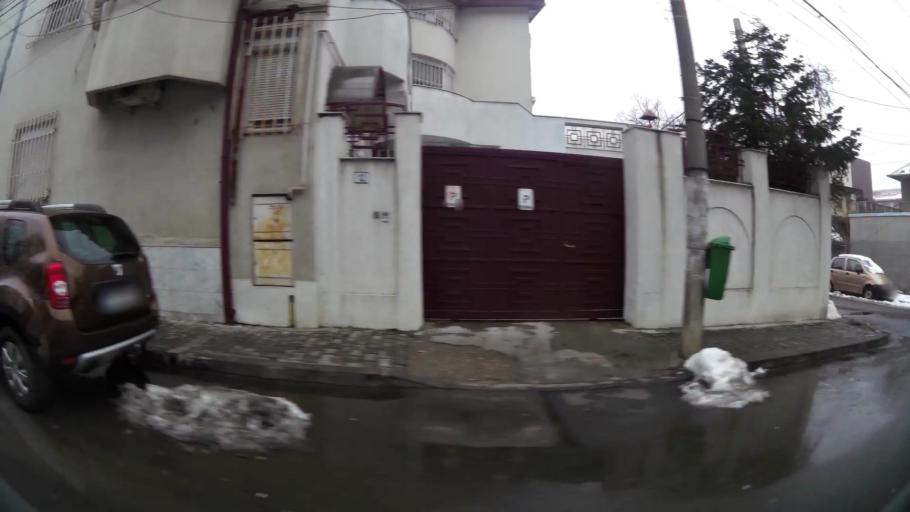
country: RO
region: Ilfov
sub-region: Comuna Chiajna
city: Rosu
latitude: 44.4495
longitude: 26.0554
